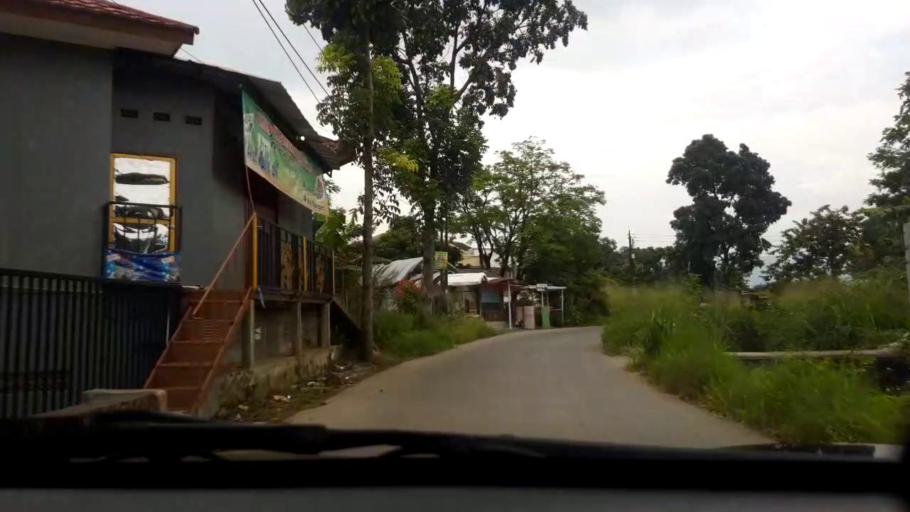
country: ID
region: West Java
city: Cileunyi
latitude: -6.9458
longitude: 107.7151
